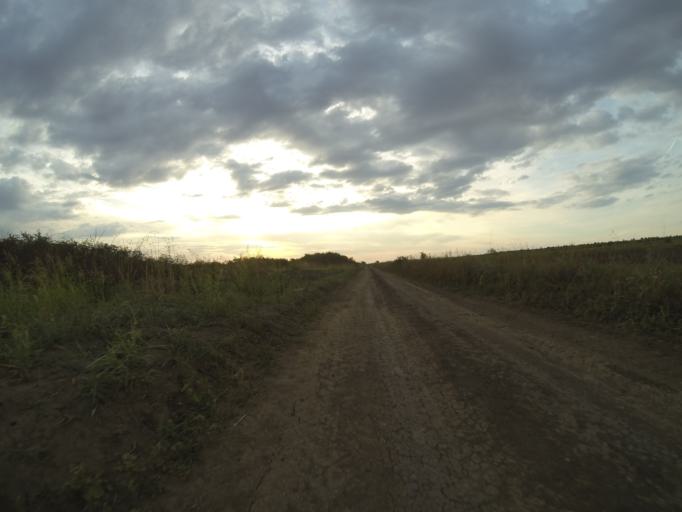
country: RO
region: Dolj
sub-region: Comuna Ceratu
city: Ceratu
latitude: 44.1006
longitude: 23.6758
